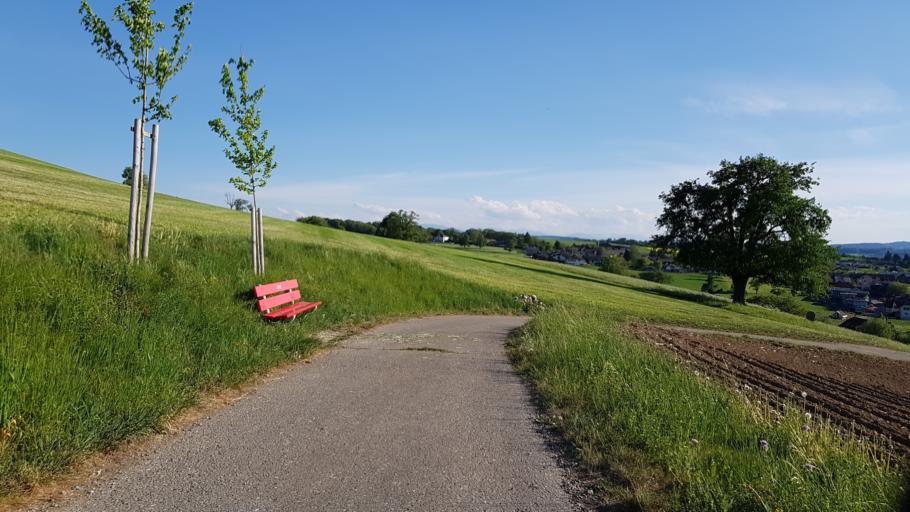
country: CH
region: Aargau
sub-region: Bezirk Bremgarten
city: Sarmenstorf
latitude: 47.2997
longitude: 8.2505
